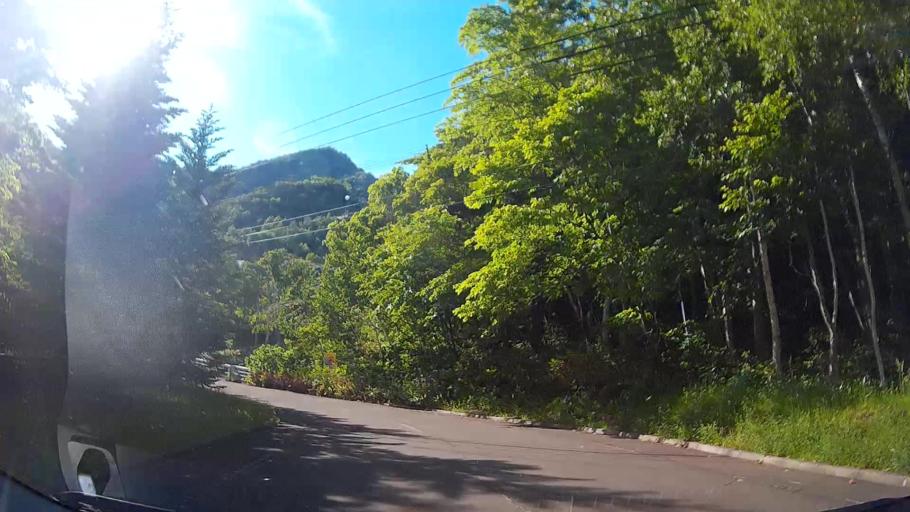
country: JP
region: Hokkaido
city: Sapporo
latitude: 42.9825
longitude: 141.1582
